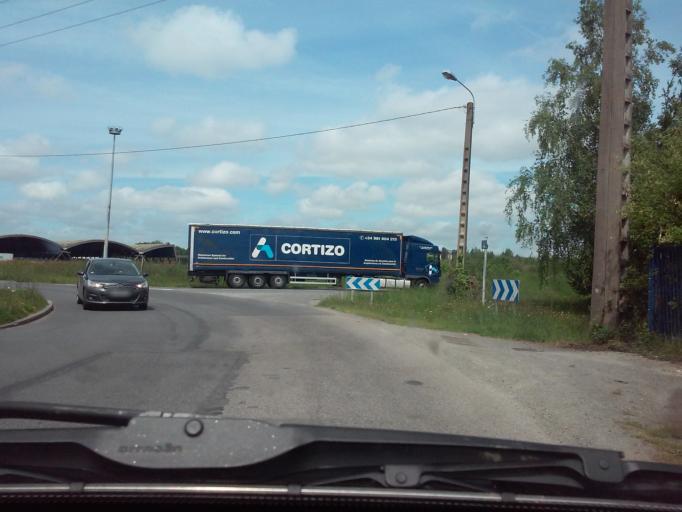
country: FR
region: Brittany
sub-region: Departement d'Ille-et-Vilaine
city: Beauce
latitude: 48.3341
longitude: -1.1667
